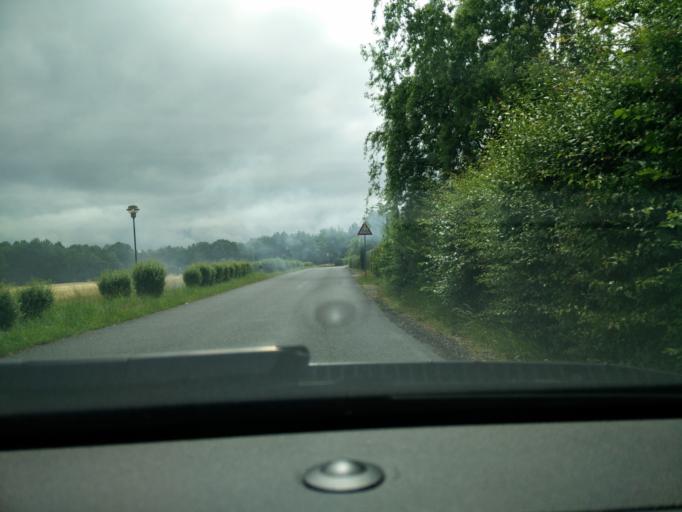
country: DE
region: Saxony
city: Bad Lausick
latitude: 51.1528
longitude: 12.6610
